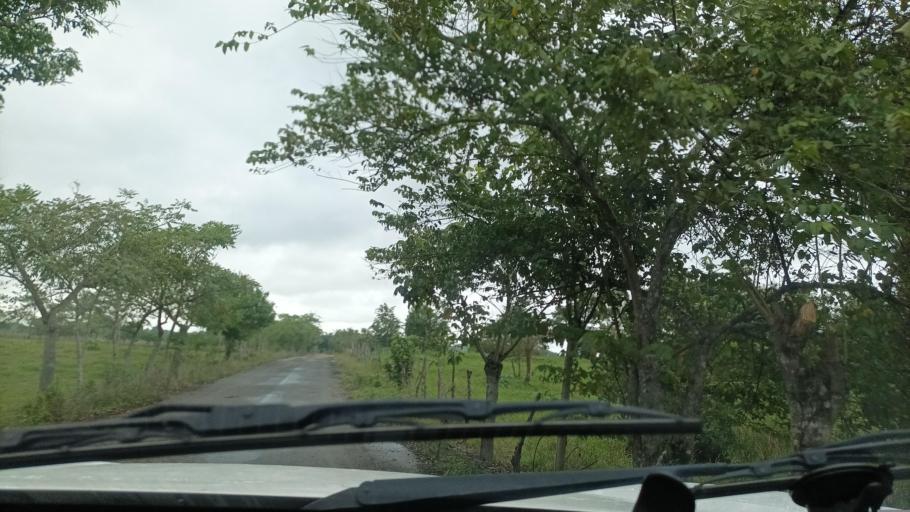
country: MX
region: Veracruz
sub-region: Moloacan
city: Cuichapa
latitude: 17.7724
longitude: -94.3880
